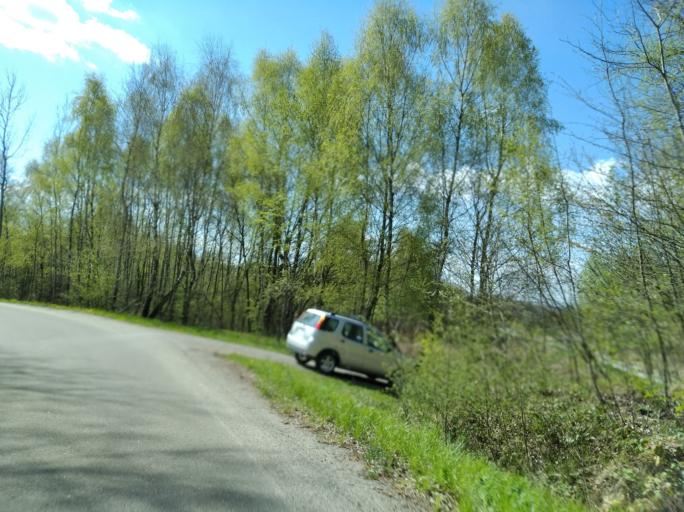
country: PL
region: Subcarpathian Voivodeship
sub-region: Powiat brzozowski
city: Golcowa
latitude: 49.7938
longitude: 22.0307
